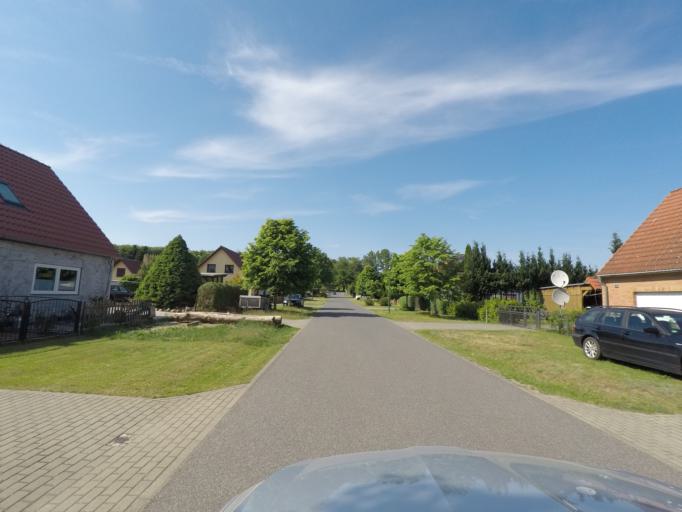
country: DE
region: Brandenburg
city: Melchow
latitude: 52.8644
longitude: 13.7203
